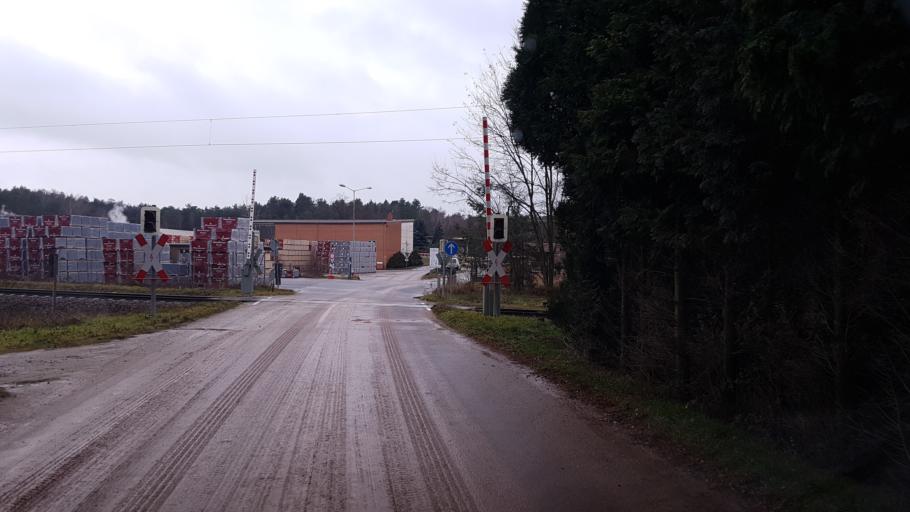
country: DE
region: Brandenburg
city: Calau
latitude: 51.7116
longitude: 13.9907
